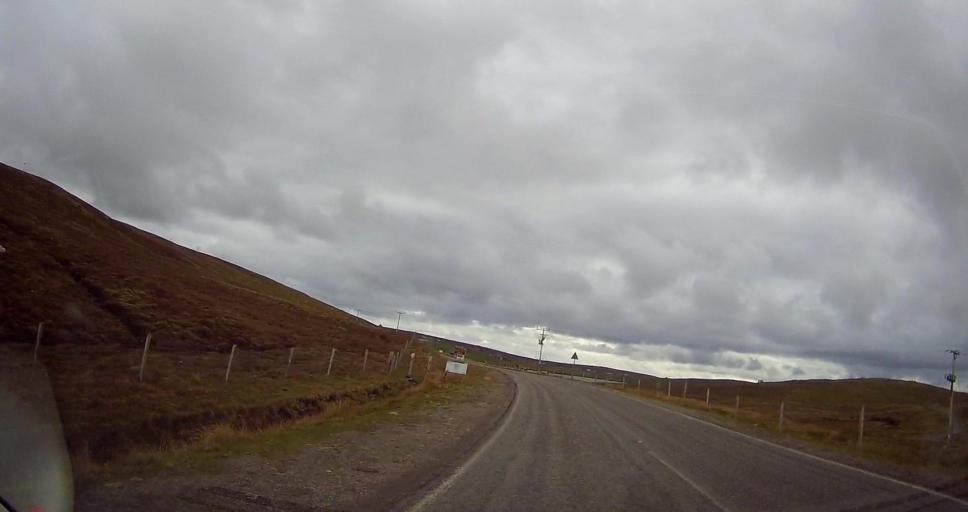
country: GB
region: Scotland
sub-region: Shetland Islands
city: Shetland
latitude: 60.6049
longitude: -1.0950
